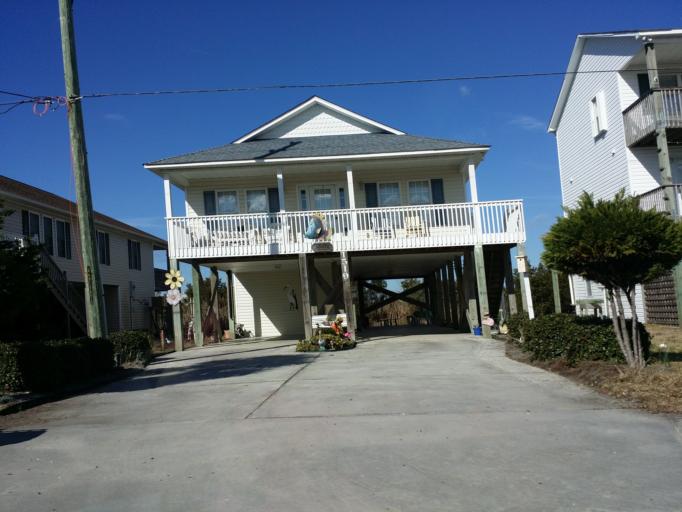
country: US
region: North Carolina
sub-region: Pender County
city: Surf City
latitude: 34.4415
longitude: -77.5205
